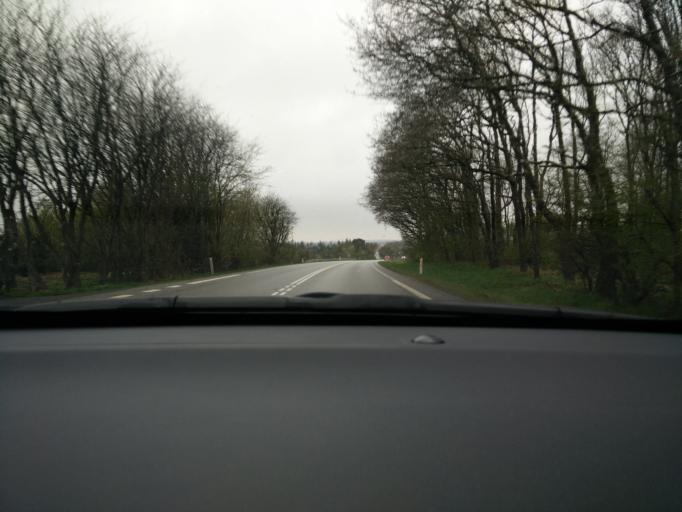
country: DK
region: Central Jutland
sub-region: Skive Kommune
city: Hojslev
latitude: 56.5398
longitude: 9.1396
